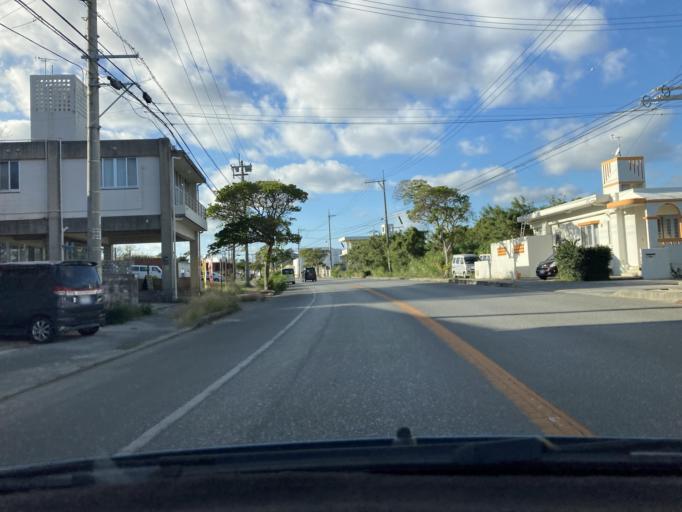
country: JP
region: Okinawa
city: Katsuren-haebaru
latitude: 26.3432
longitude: 127.8778
